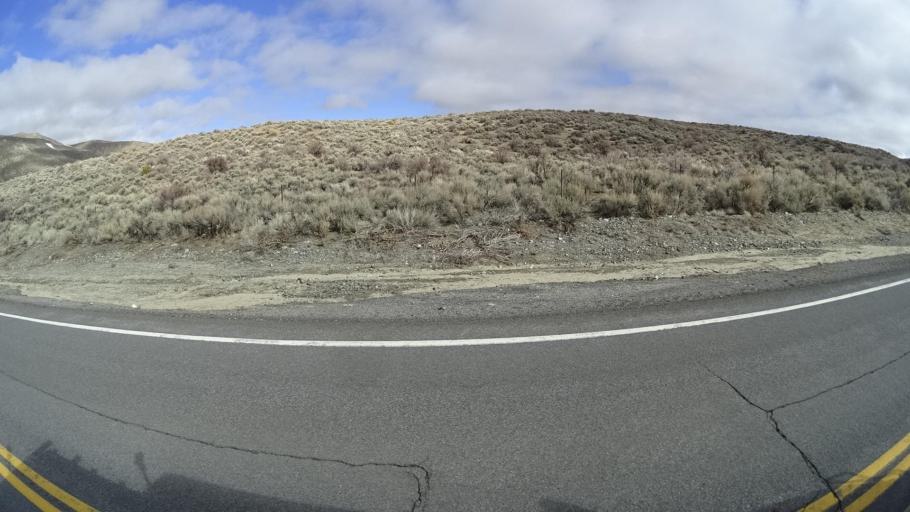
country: US
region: Nevada
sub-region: Washoe County
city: Cold Springs
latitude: 39.8048
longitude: -119.9270
